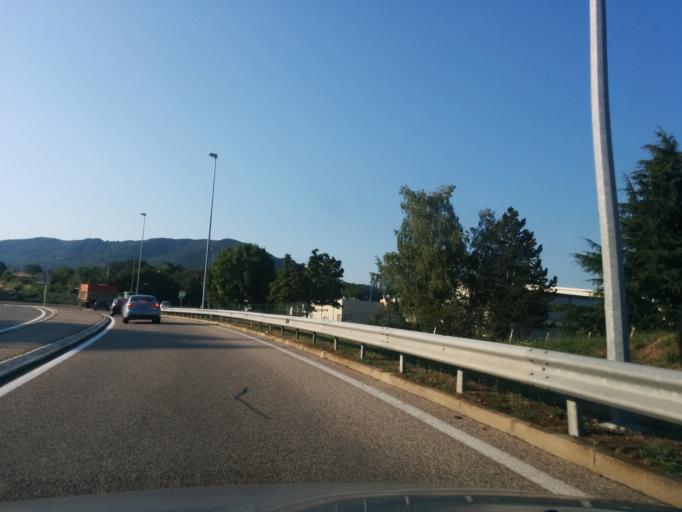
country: FR
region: Rhone-Alpes
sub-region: Departement de l'Isere
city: Saint-Cassien
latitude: 45.3588
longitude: 5.5692
